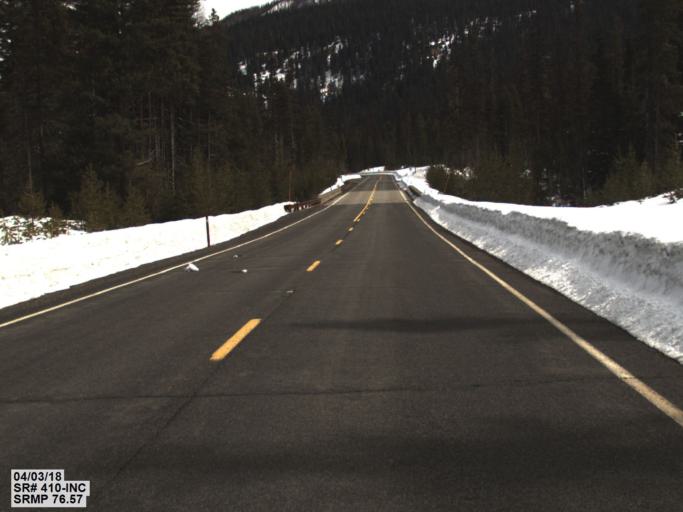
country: US
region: Washington
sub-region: Kittitas County
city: Cle Elum
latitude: 46.9148
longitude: -121.3876
